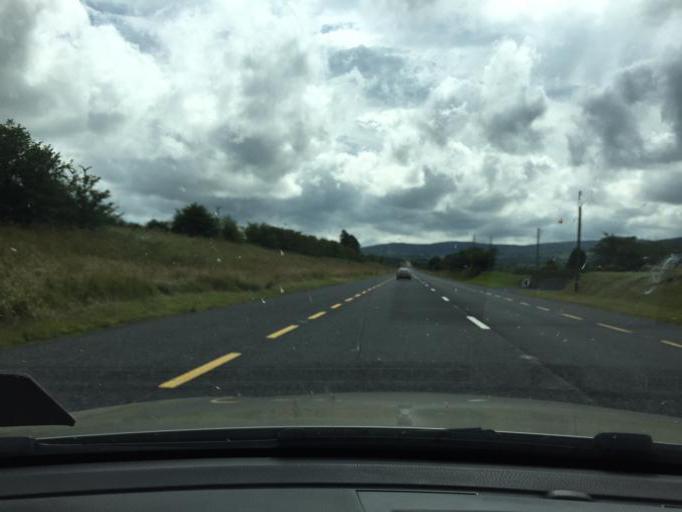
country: IE
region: Munster
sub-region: Waterford
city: Dungarvan
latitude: 52.1784
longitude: -7.4980
